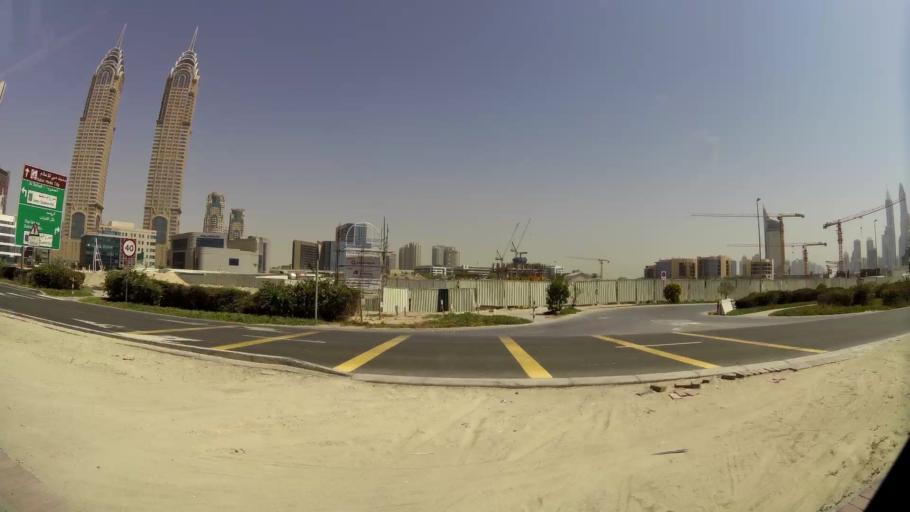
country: AE
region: Dubai
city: Dubai
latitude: 25.1027
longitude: 55.1655
